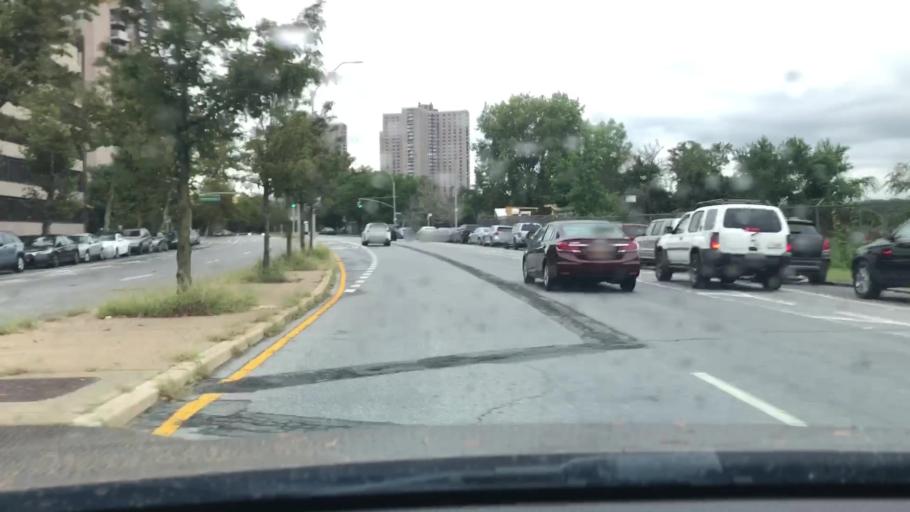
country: US
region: New York
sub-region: Bronx
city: Eastchester
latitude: 40.8727
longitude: -73.8243
